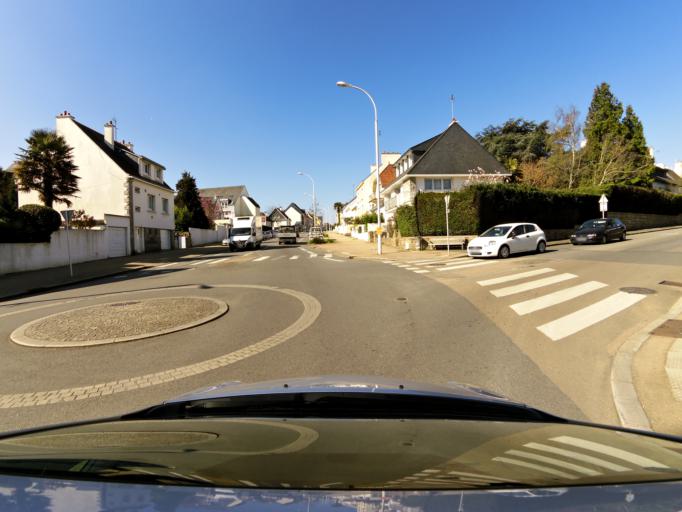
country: FR
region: Brittany
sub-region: Departement du Morbihan
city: Lorient
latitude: 47.7473
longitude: -3.3764
